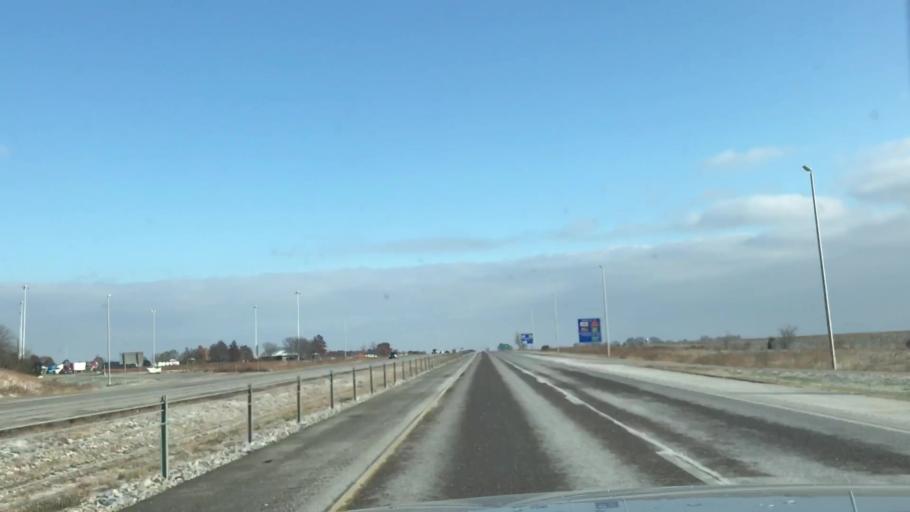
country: US
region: Illinois
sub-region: Madison County
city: Worden
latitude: 38.8685
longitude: -89.8525
